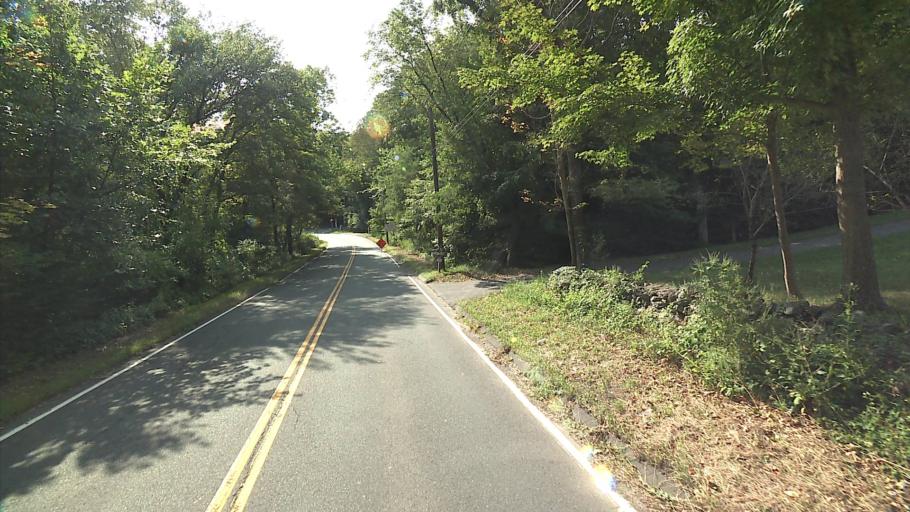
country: US
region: Connecticut
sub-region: Fairfield County
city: Westport
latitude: 41.2300
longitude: -73.3189
